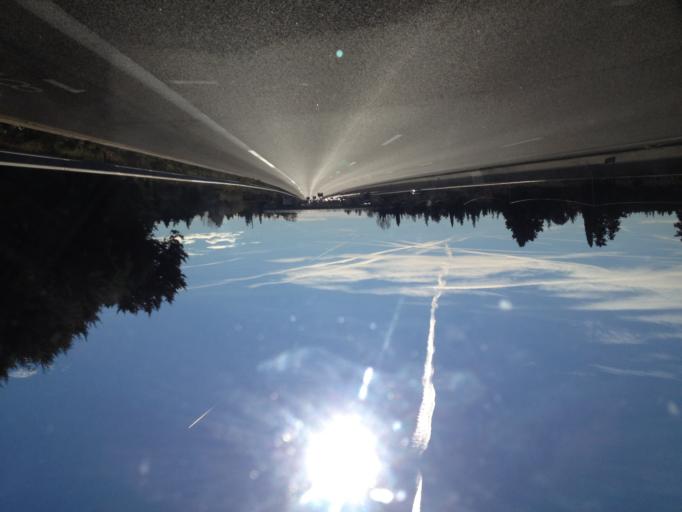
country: FR
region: Provence-Alpes-Cote d'Azur
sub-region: Departement du Vaucluse
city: Sorgues
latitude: 44.0026
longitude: 4.8884
